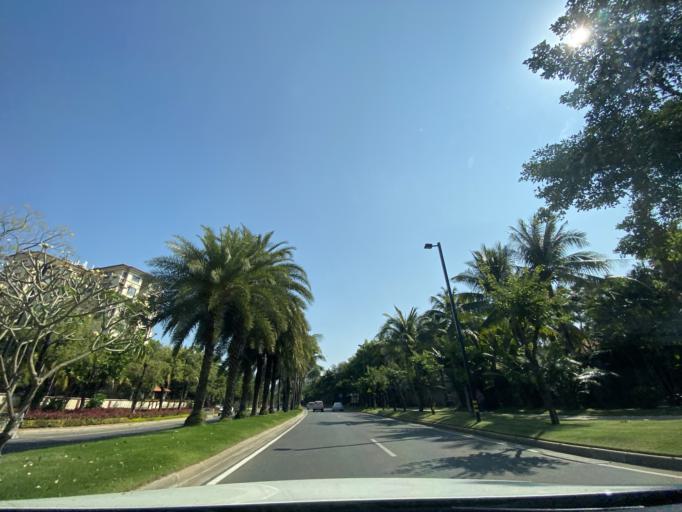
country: CN
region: Hainan
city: Yingzhou
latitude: 18.3972
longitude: 109.8579
